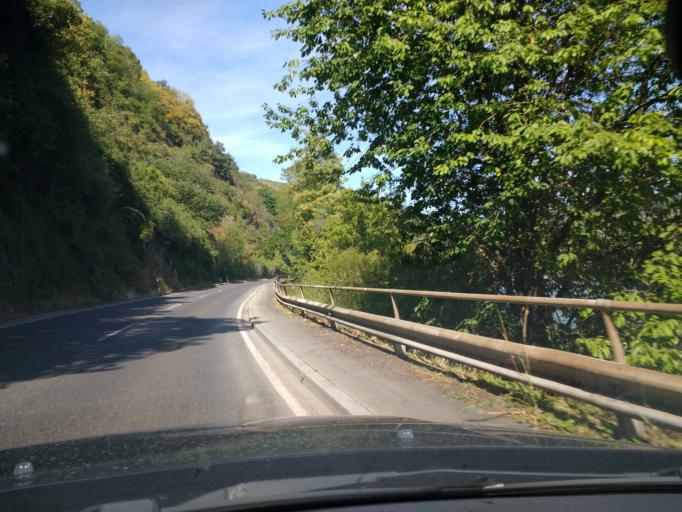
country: DE
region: Rheinland-Pfalz
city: Ayl
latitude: 49.6191
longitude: 6.5604
